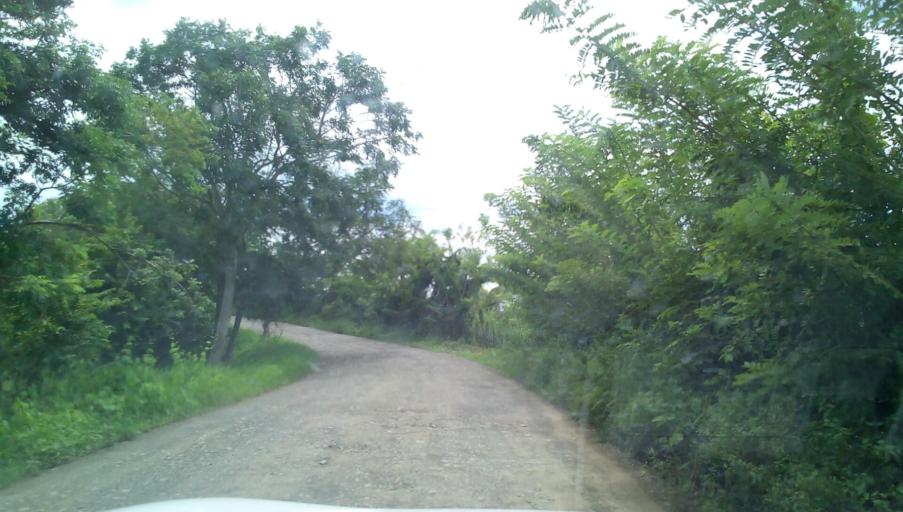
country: MX
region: Veracruz
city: Tepetzintla
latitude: 21.1439
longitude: -97.8548
